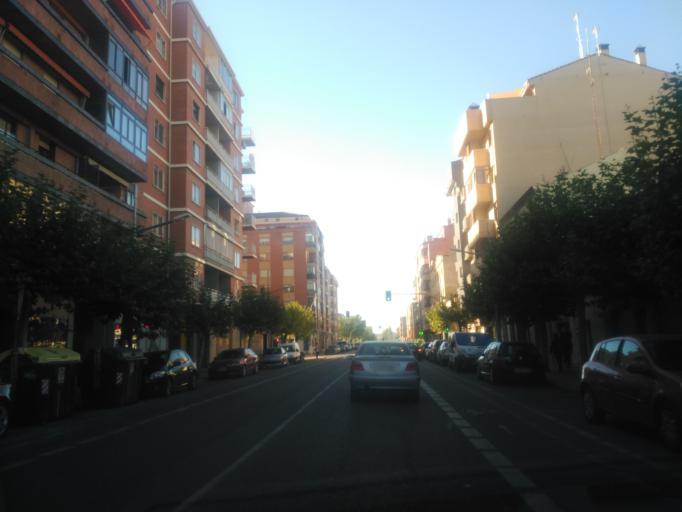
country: ES
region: Castille and Leon
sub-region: Provincia de Burgos
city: Aranda de Duero
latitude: 41.6664
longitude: -3.6912
